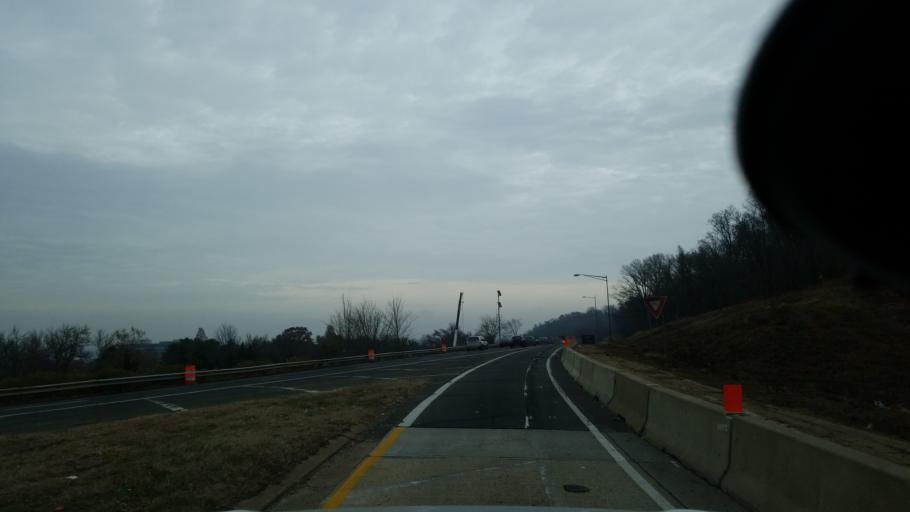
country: US
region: Maryland
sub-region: Prince George's County
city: Glassmanor
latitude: 38.8387
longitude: -77.0086
